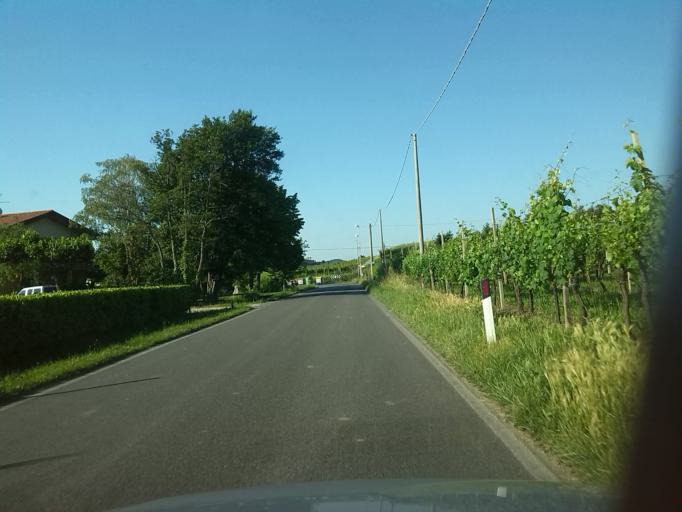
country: IT
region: Friuli Venezia Giulia
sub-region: Provincia di Udine
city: Prepotto
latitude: 46.0594
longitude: 13.4562
